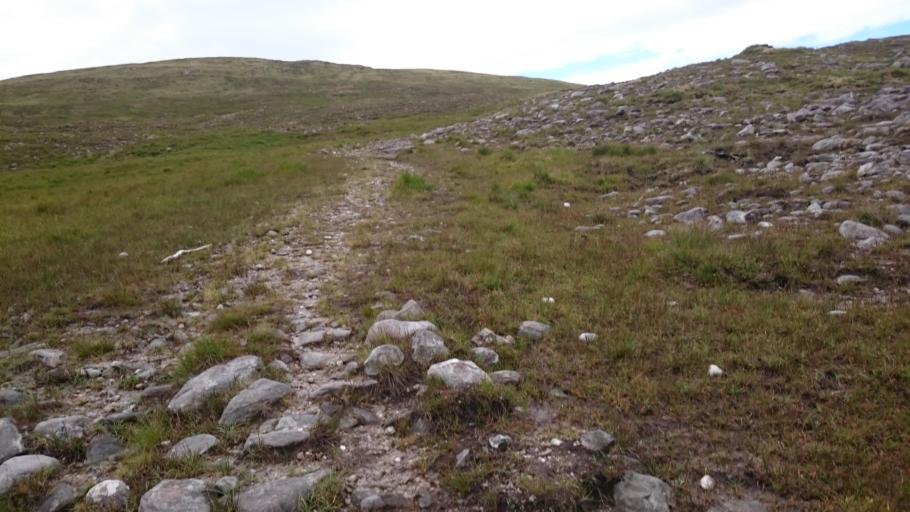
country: IE
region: Connaught
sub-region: Maigh Eo
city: Westport
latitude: 53.9978
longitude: -9.6050
